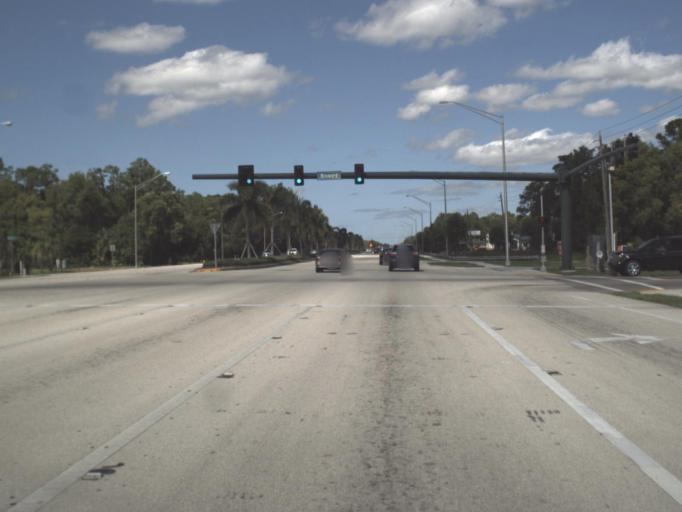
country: US
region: Florida
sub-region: Collier County
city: Naples Manor
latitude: 26.0822
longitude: -81.7250
